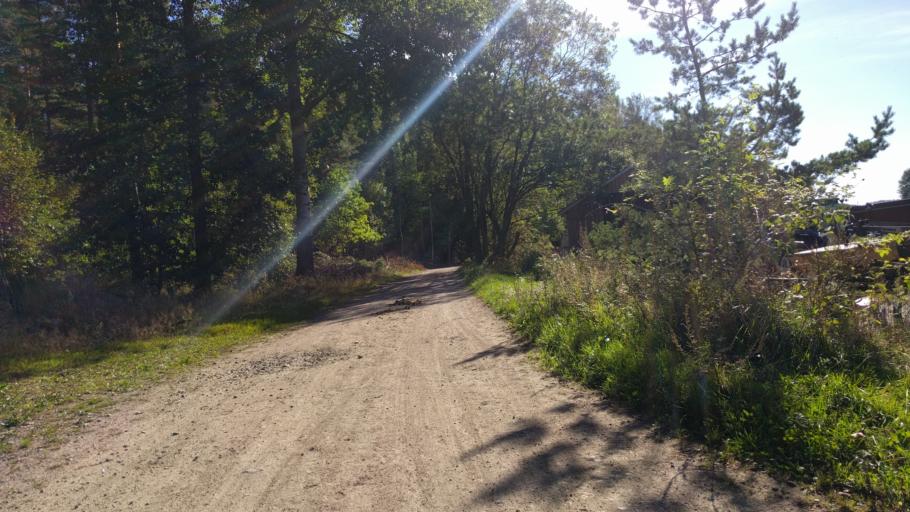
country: SE
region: Stockholm
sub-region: Vallentuna Kommun
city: Vallentuna
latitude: 59.4882
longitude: 18.1201
